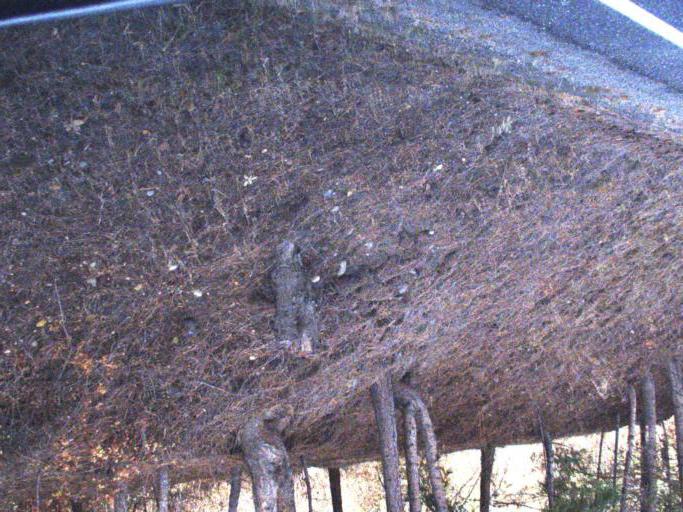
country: US
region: Washington
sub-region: Stevens County
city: Kettle Falls
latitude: 48.6678
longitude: -118.0441
